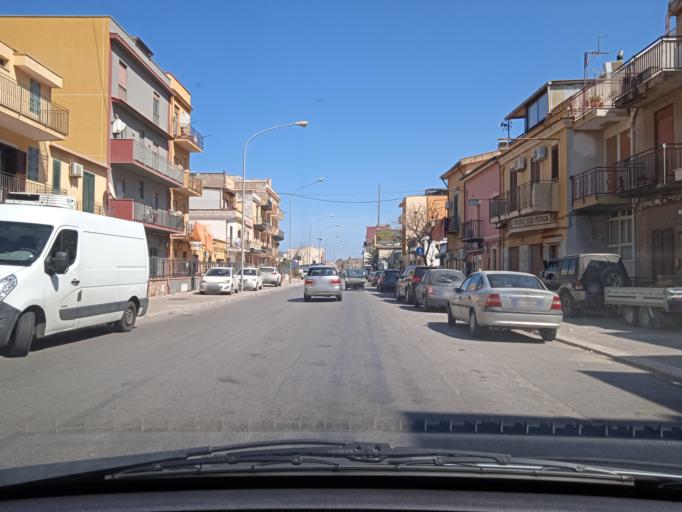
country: IT
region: Sicily
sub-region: Palermo
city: Ciaculli
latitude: 38.0977
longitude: 13.4153
